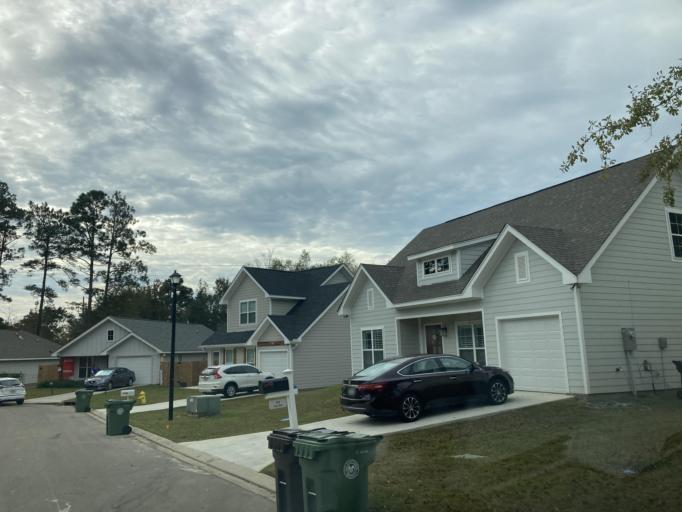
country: US
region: Mississippi
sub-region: Lamar County
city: West Hattiesburg
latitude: 31.2826
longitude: -89.3499
